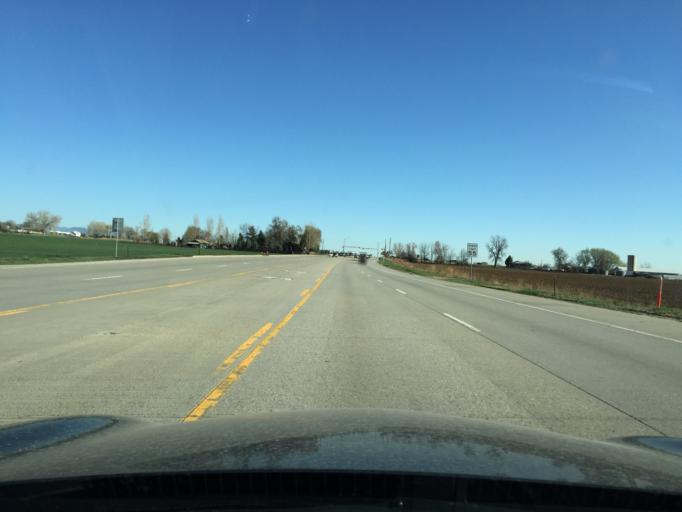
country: US
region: Colorado
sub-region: Boulder County
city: Erie
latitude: 40.0833
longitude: -105.1026
